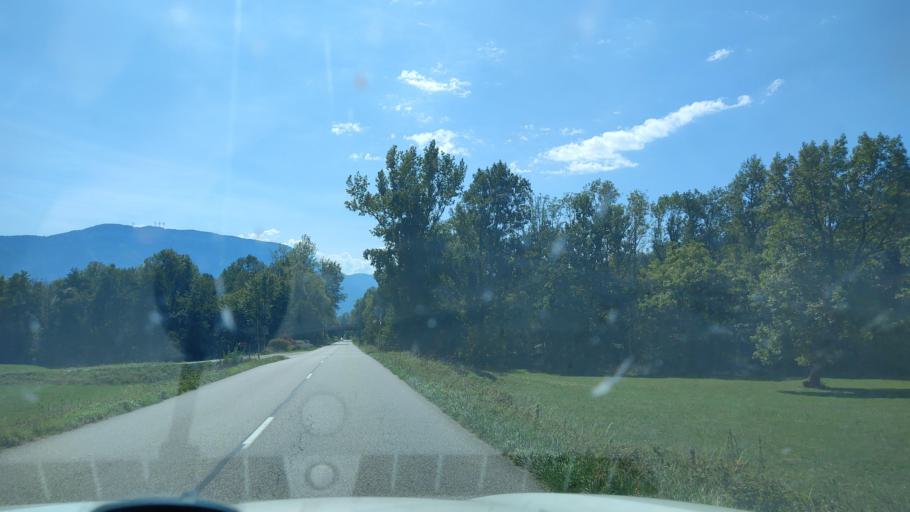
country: FR
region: Rhone-Alpes
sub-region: Departement de la Savoie
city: Novalaise
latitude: 45.5799
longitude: 5.7933
